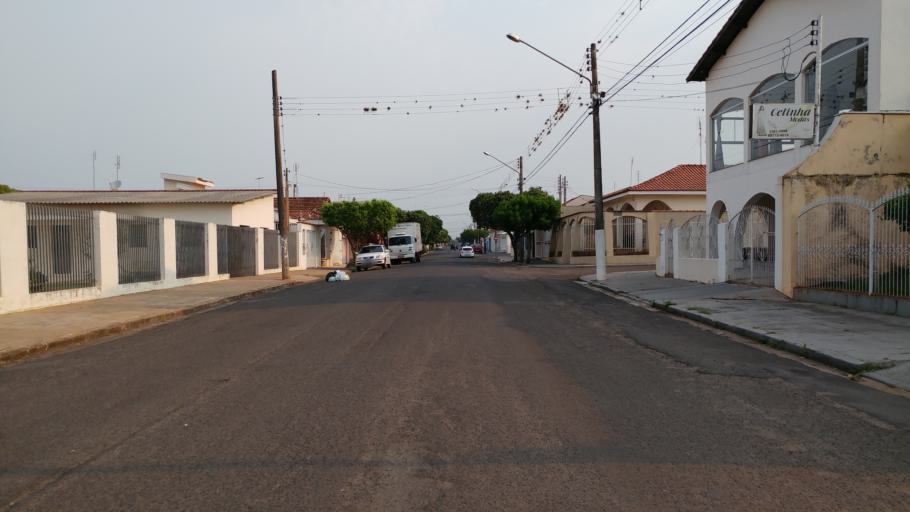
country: BR
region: Sao Paulo
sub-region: Paraguacu Paulista
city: Paraguacu Paulista
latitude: -22.4215
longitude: -50.5772
